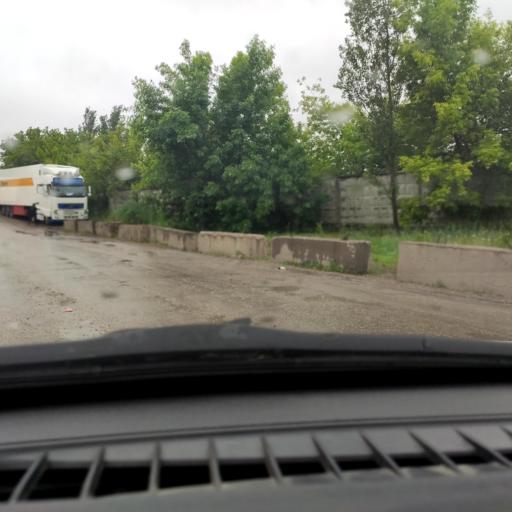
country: RU
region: Samara
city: Tol'yatti
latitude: 53.5717
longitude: 49.3678
